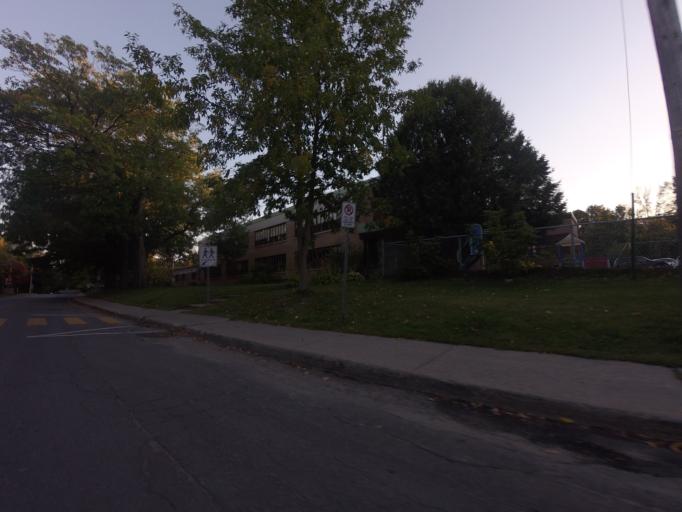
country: CA
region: Quebec
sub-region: Monteregie
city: Hudson
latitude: 45.4566
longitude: -74.1378
